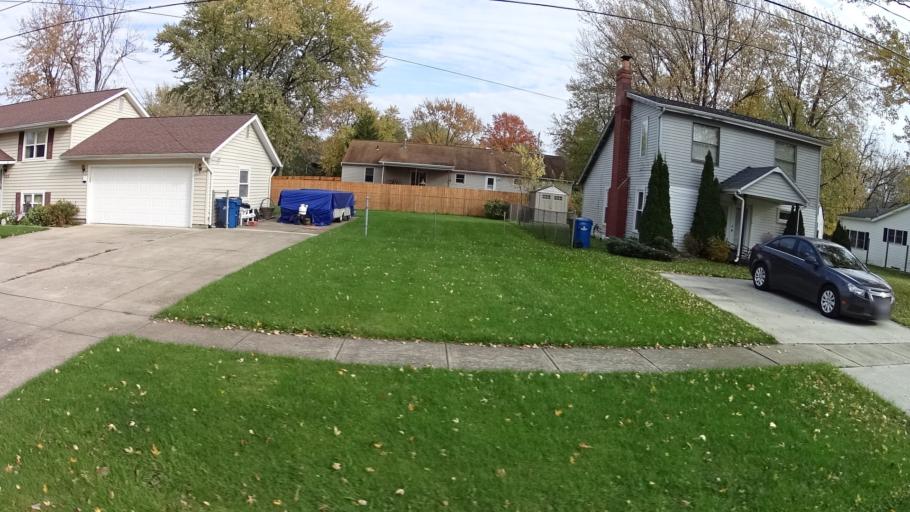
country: US
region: Ohio
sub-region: Lorain County
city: Sheffield Lake
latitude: 41.4910
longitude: -82.0964
